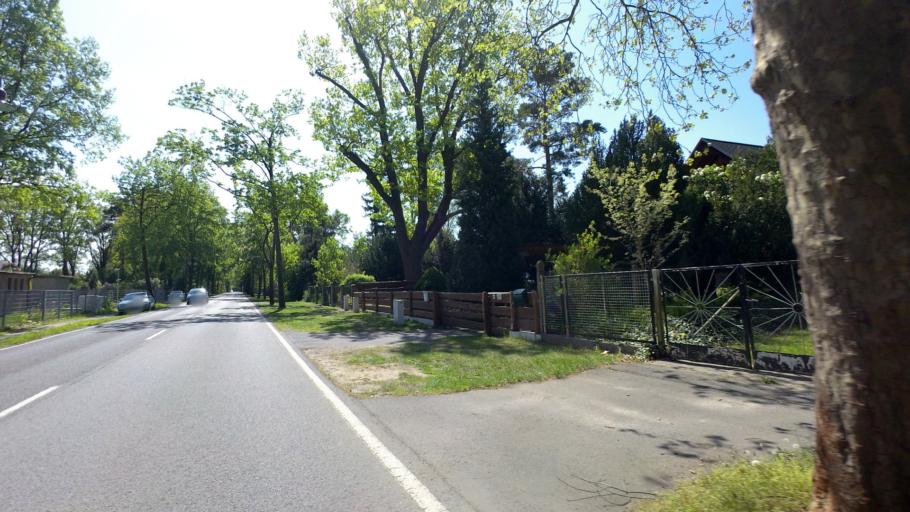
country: DE
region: Brandenburg
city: Bestensee
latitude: 52.2342
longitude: 13.6676
